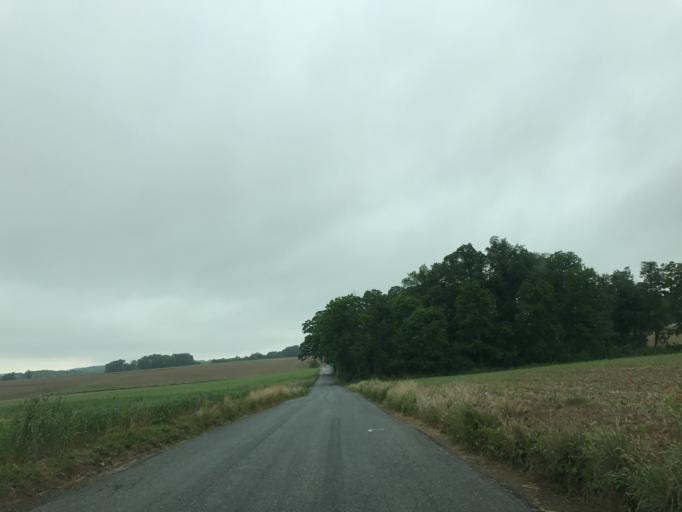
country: US
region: Pennsylvania
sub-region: York County
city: Susquehanna Trails
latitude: 39.7212
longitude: -76.4685
